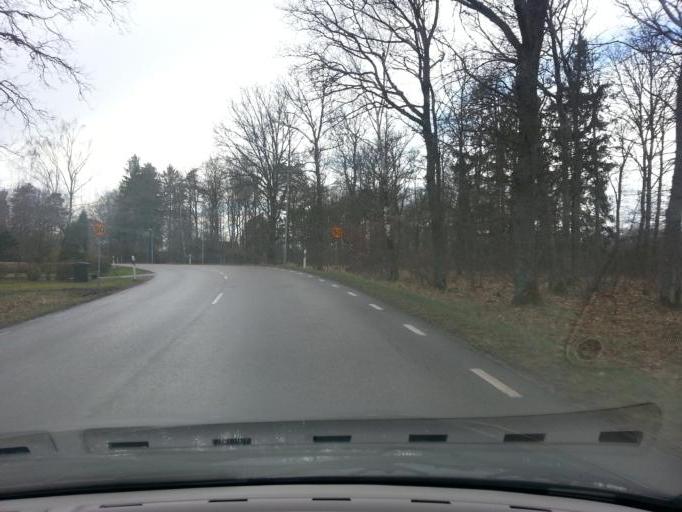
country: SE
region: Skane
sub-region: Klippans Kommun
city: Ljungbyhed
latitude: 56.0814
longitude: 13.2493
